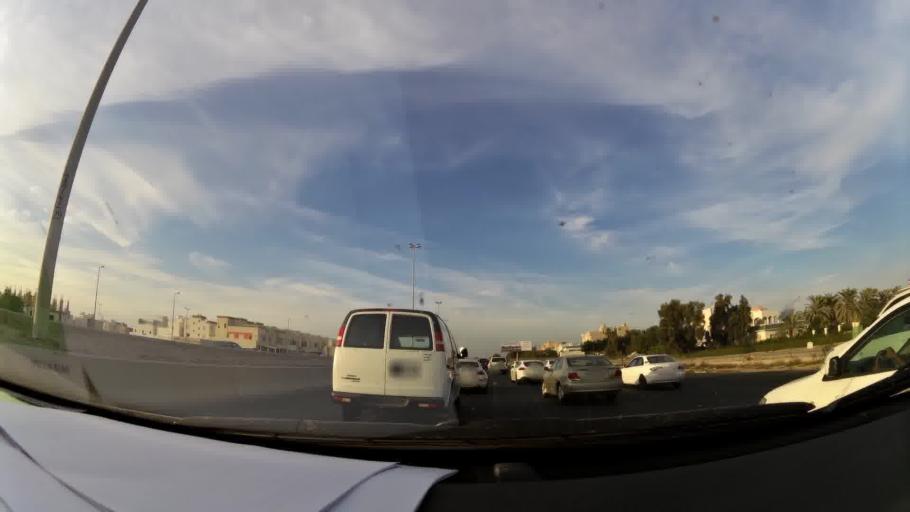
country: KW
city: Al Funaytis
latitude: 29.2212
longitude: 48.1006
